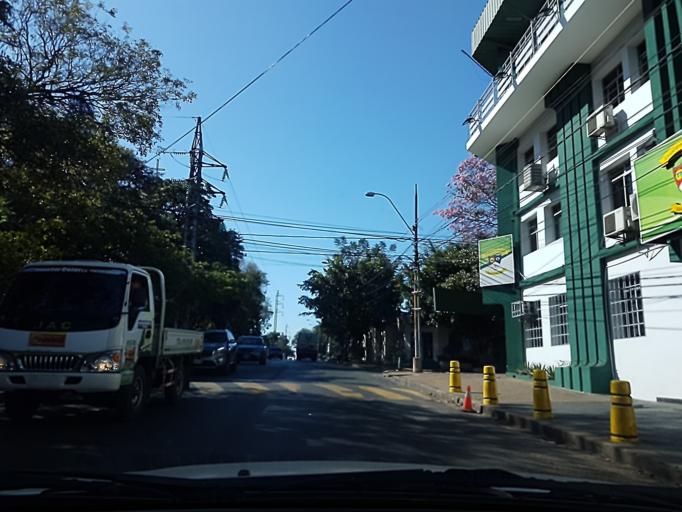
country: PY
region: Central
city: Fernando de la Mora
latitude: -25.2986
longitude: -57.5639
